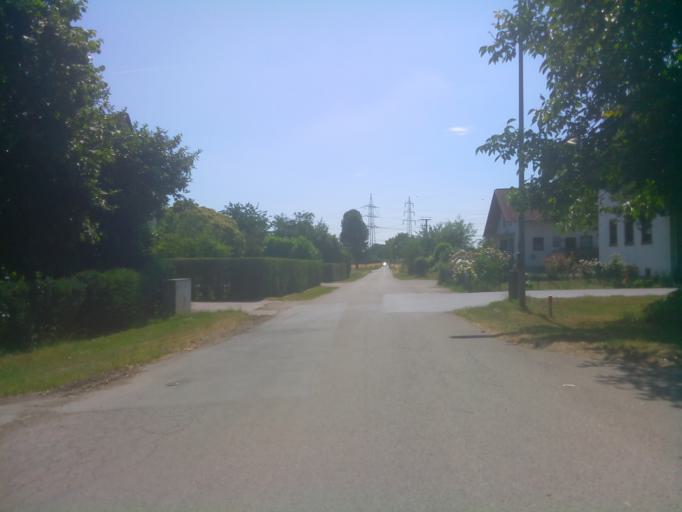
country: DE
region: Baden-Wuerttemberg
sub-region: Karlsruhe Region
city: Hemsbach
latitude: 49.5783
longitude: 8.6193
